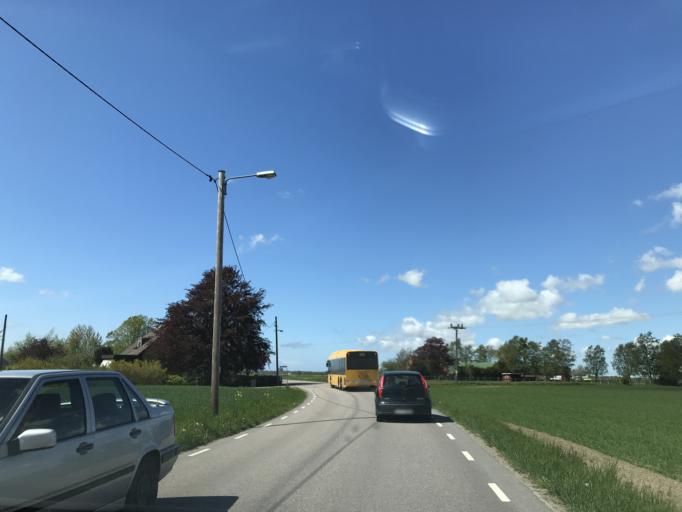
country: SE
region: Skane
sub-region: Helsingborg
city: Barslov
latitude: 55.9872
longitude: 12.8380
